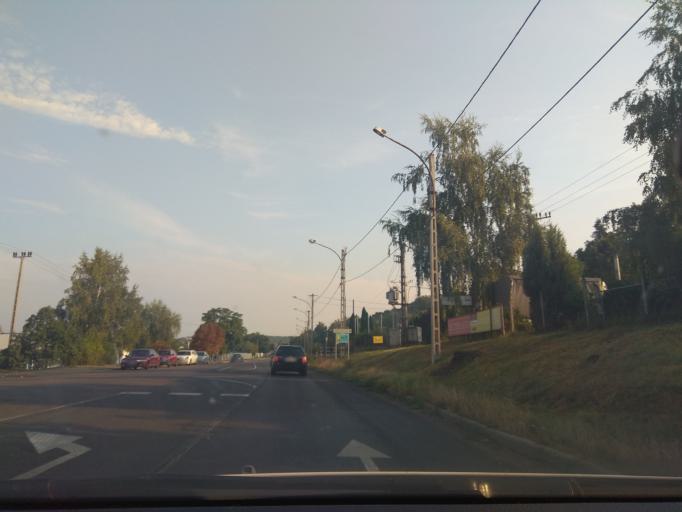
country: HU
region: Heves
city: Eger
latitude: 47.8821
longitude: 20.3990
